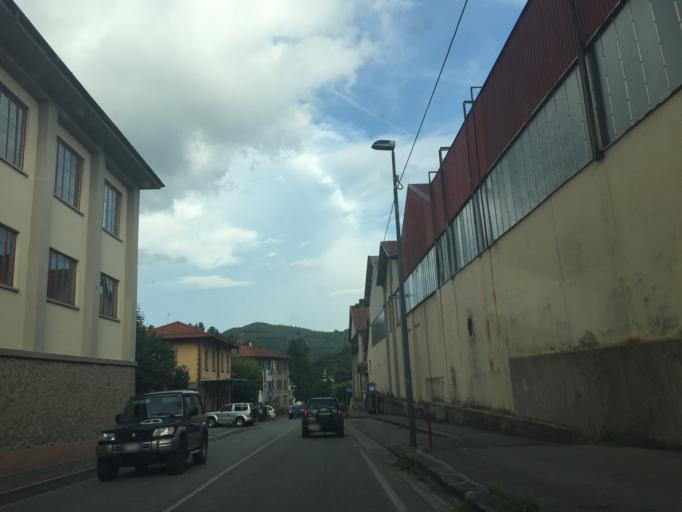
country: IT
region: Tuscany
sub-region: Provincia di Pistoia
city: Campo Tizzoro
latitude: 44.0383
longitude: 10.8663
